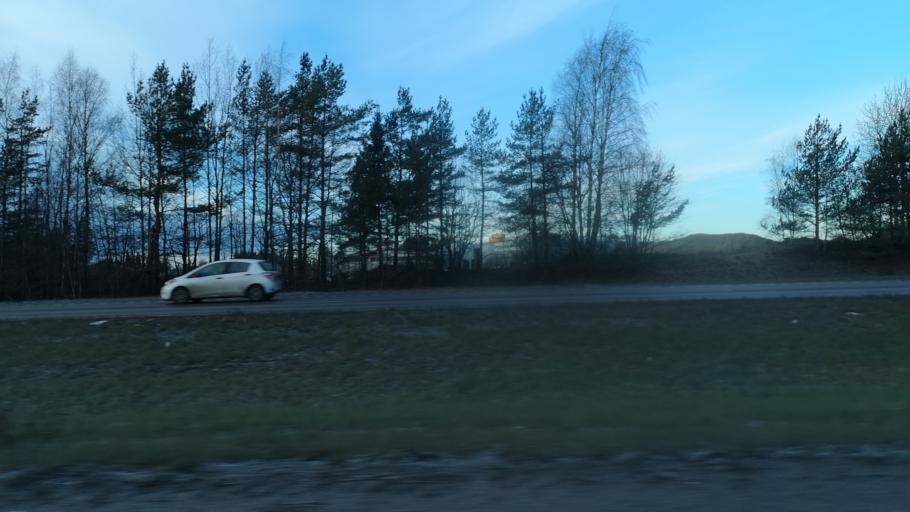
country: FI
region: Uusimaa
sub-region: Helsinki
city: Vantaa
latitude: 60.2983
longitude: 25.0958
